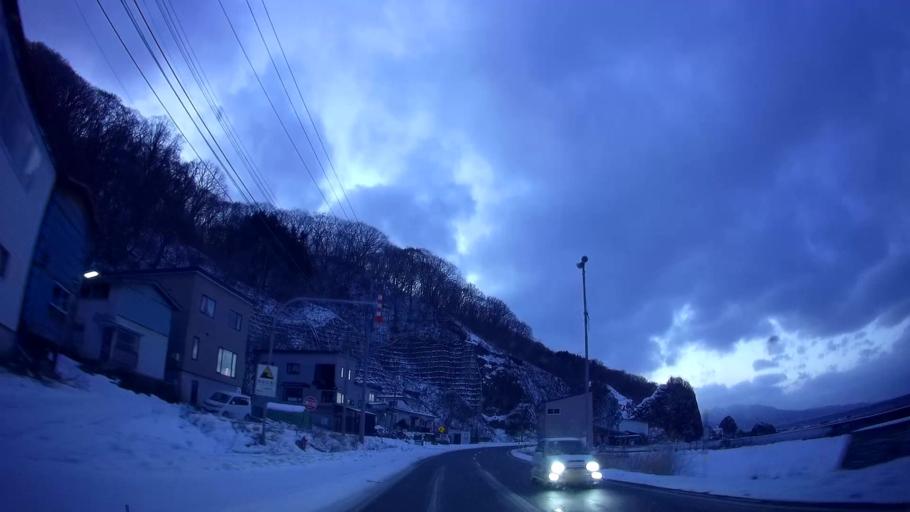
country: JP
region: Hokkaido
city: Hakodate
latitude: 41.8911
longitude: 141.0529
